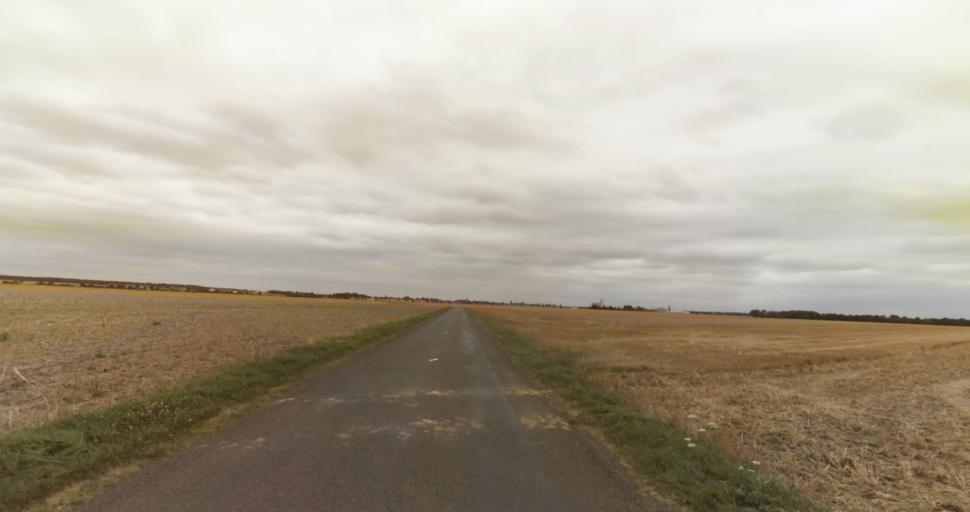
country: FR
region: Haute-Normandie
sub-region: Departement de l'Eure
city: Marcilly-sur-Eure
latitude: 48.9249
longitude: 1.2716
